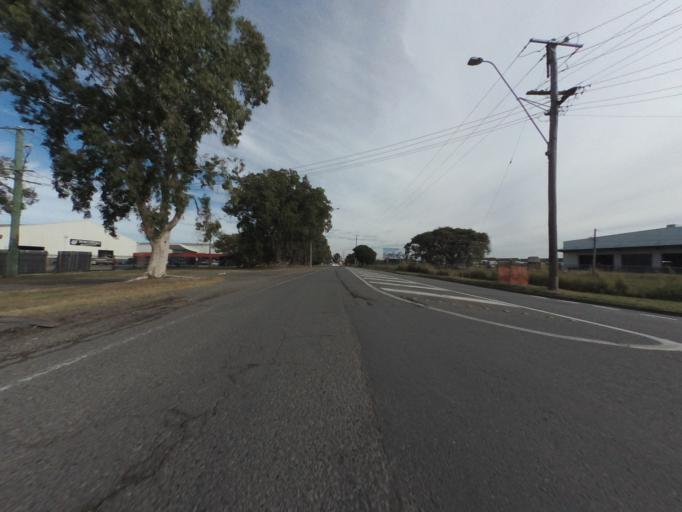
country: AU
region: Queensland
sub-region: Brisbane
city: Cannon Hill
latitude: -27.4304
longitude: 153.1088
